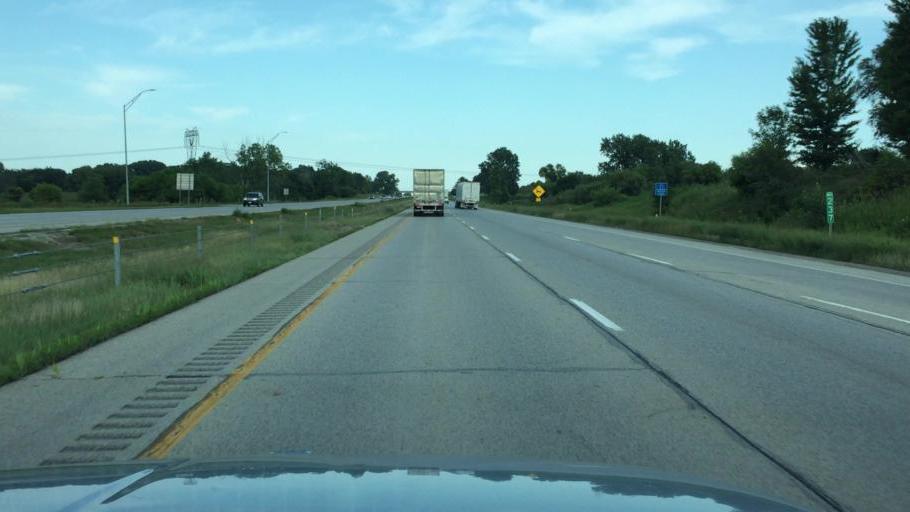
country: US
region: Iowa
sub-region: Johnson County
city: Tiffin
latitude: 41.6942
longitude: -91.6793
